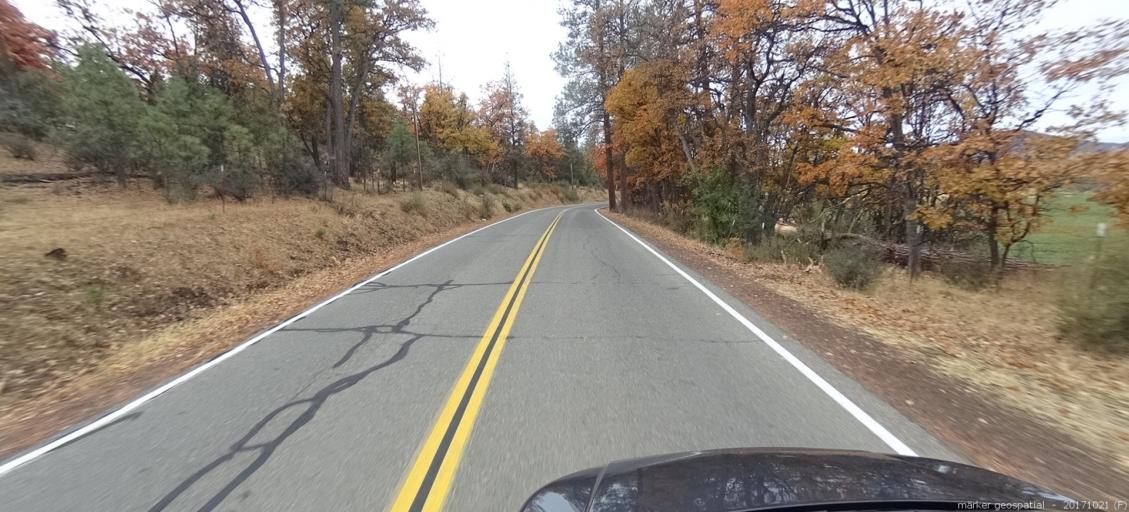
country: US
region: California
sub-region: Shasta County
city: Burney
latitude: 41.0078
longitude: -121.4250
